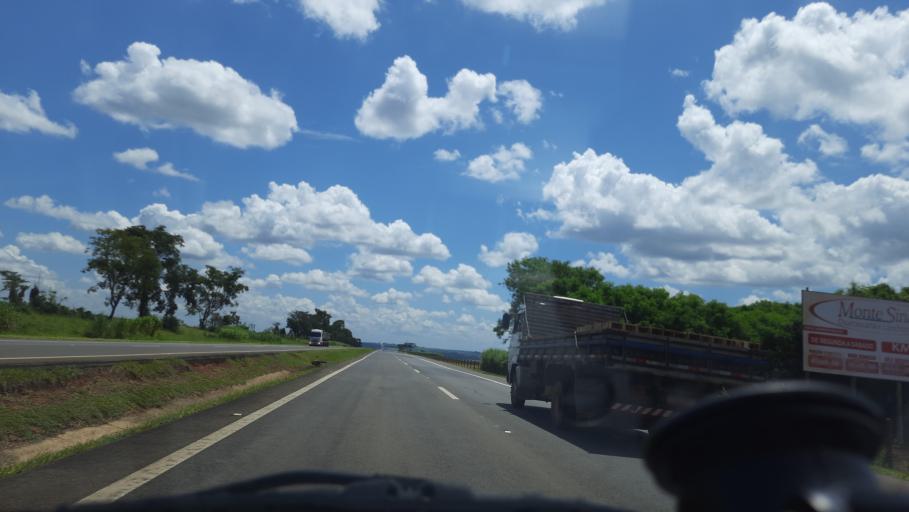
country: BR
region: Sao Paulo
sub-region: Aguai
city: Aguai
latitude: -22.0281
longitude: -47.0333
